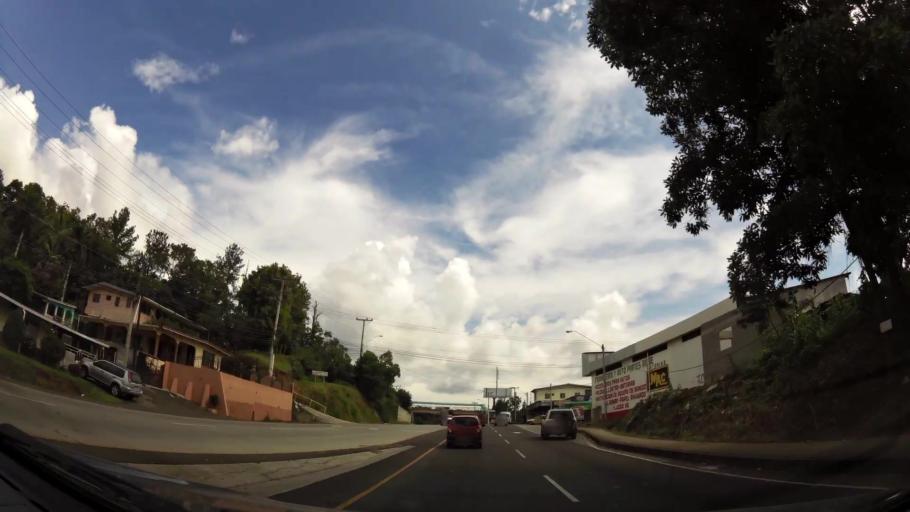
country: PA
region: Panama
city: Vista Alegre
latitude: 8.9351
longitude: -79.6871
